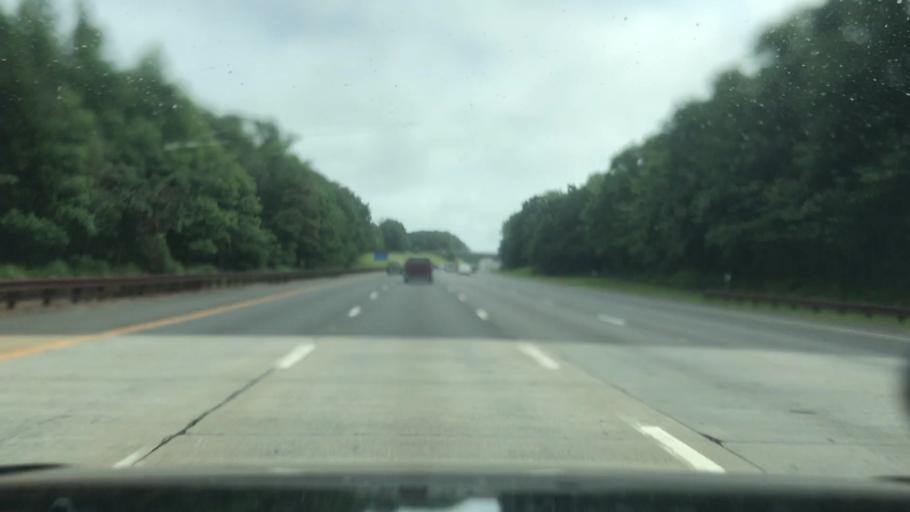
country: US
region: New Jersey
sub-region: Monmouth County
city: Shark River Hills
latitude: 40.2083
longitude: -74.0985
